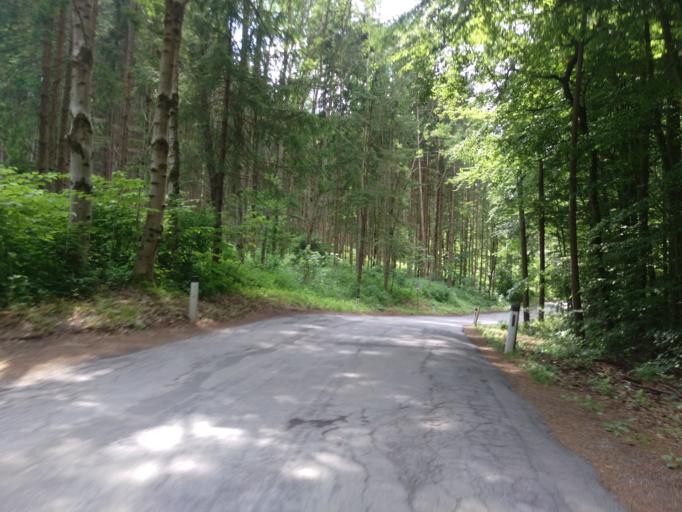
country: AT
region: Styria
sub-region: Graz Stadt
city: Mariatrost
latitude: 47.1046
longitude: 15.5018
